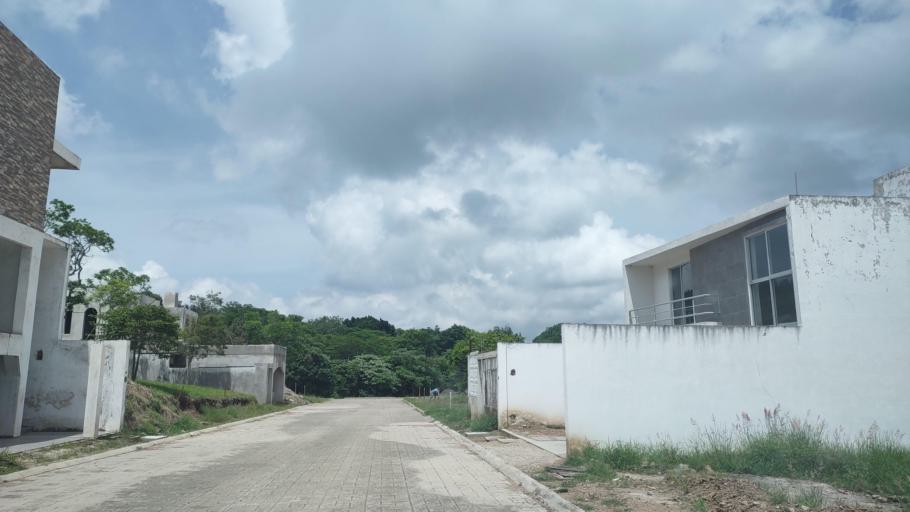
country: MX
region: Veracruz
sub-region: Emiliano Zapata
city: Jacarandas
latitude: 19.4707
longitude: -96.8504
